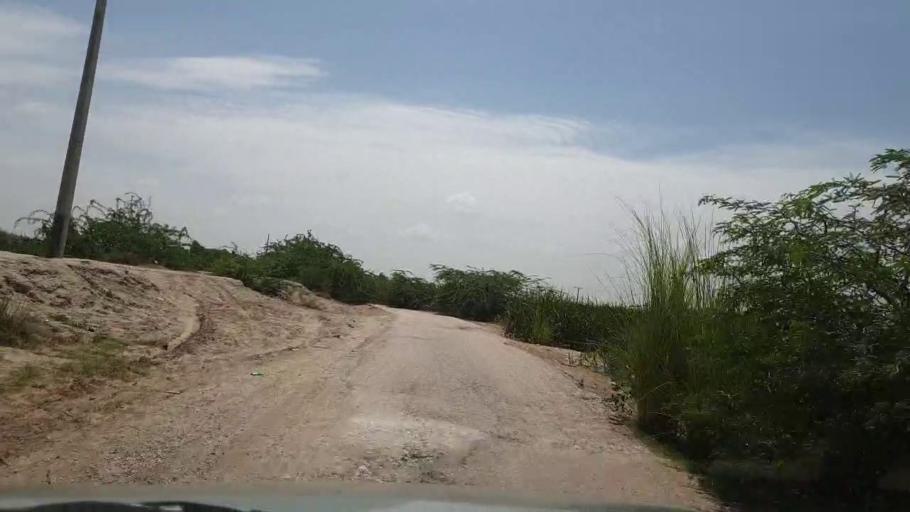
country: PK
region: Sindh
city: Bozdar
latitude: 27.0785
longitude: 68.9664
